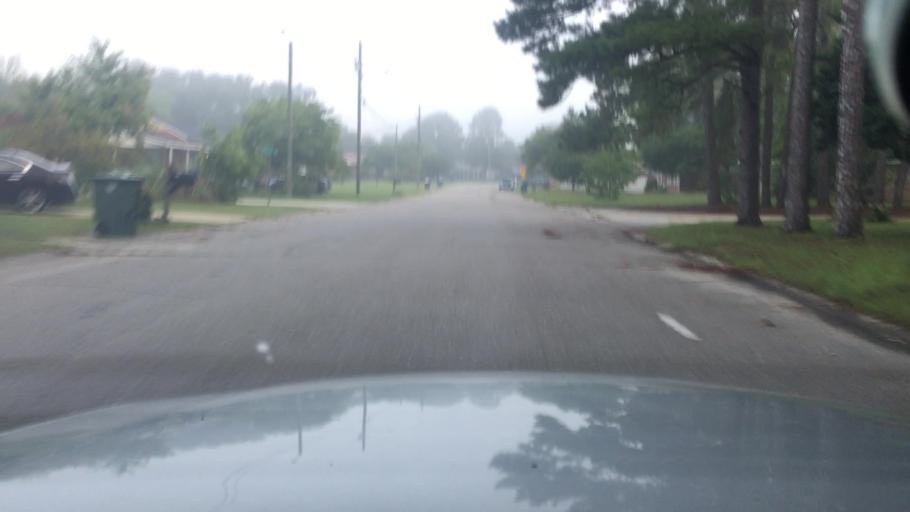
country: US
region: North Carolina
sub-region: Cumberland County
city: Hope Mills
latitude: 35.0201
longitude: -78.9444
